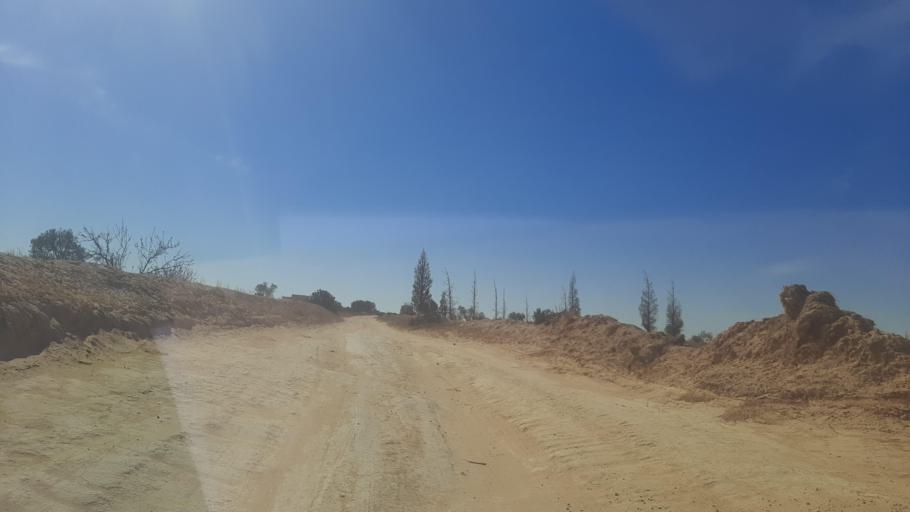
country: TN
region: Safaqis
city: Sfax
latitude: 34.8495
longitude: 10.5621
